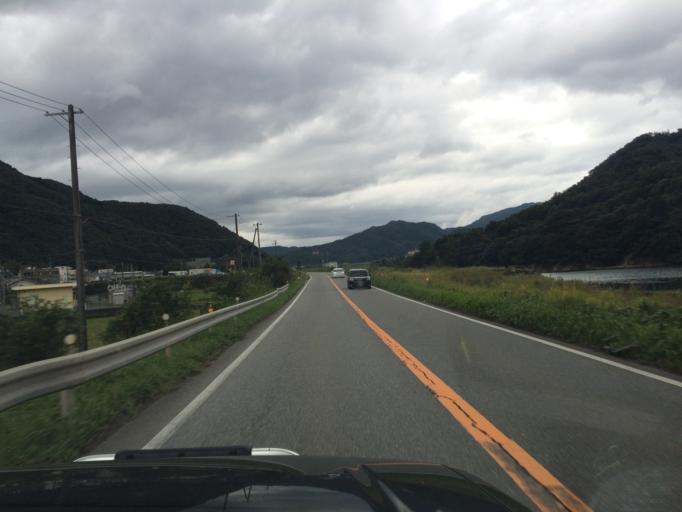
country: JP
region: Hyogo
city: Toyooka
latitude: 35.4105
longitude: 134.7791
